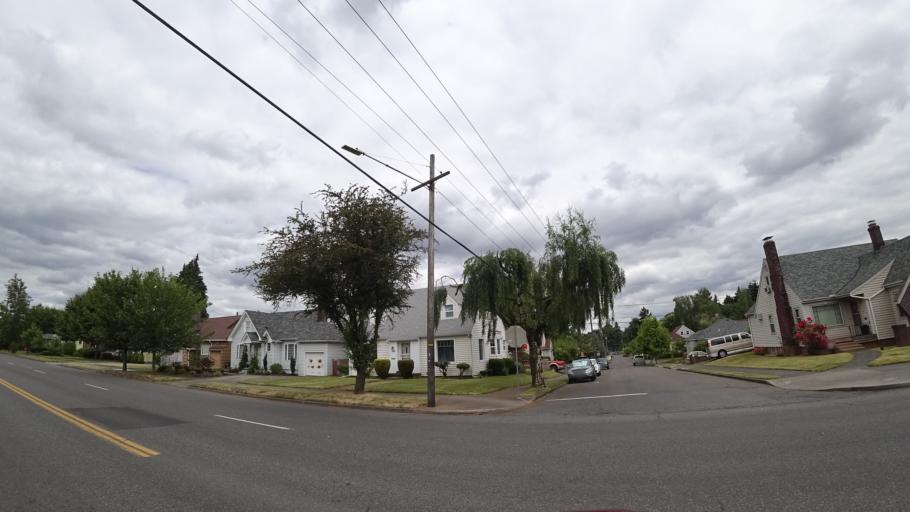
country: US
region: Oregon
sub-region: Multnomah County
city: Portland
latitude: 45.5772
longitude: -122.6707
